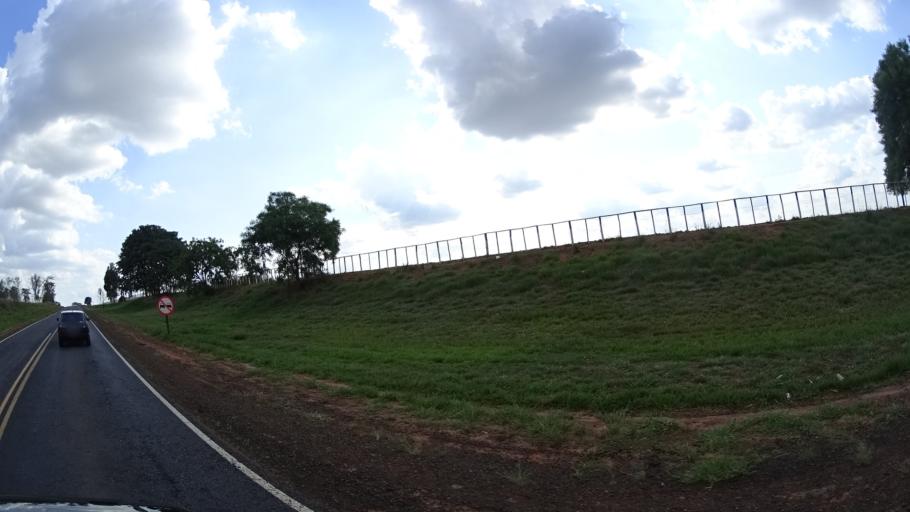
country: BR
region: Sao Paulo
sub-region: Urupes
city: Urupes
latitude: -21.1355
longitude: -49.2779
